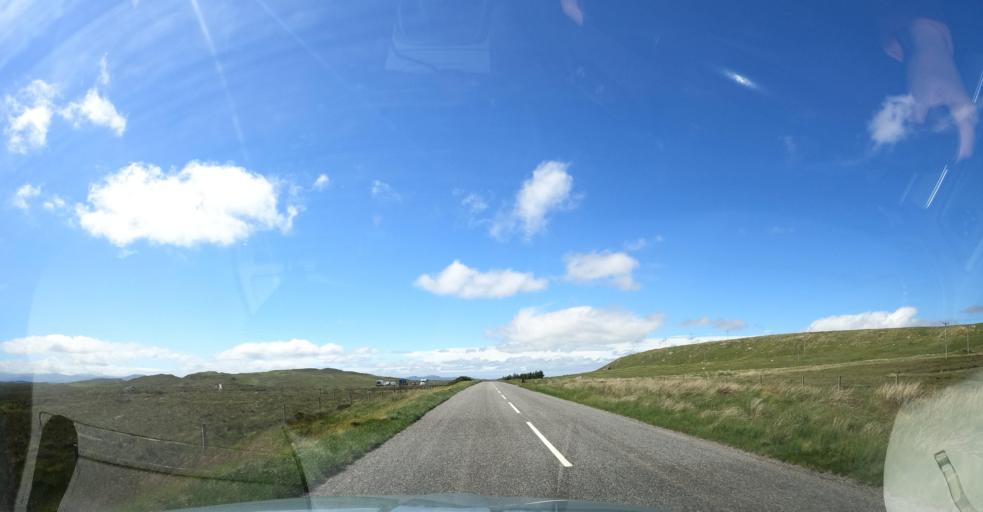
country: GB
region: Scotland
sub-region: Eilean Siar
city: Stornoway
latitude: 58.1578
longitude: -6.5205
